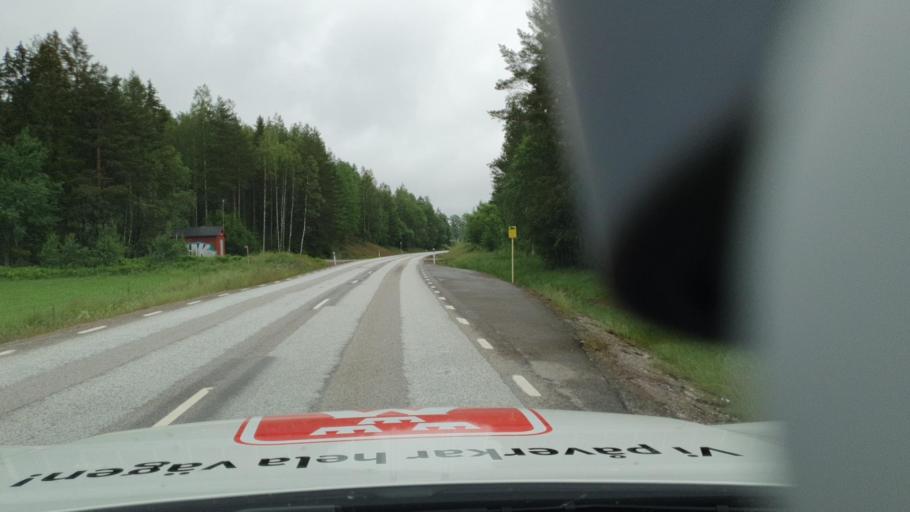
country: SE
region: Vaermland
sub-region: Kristinehamns Kommun
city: Bjorneborg
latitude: 59.2525
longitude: 14.1975
